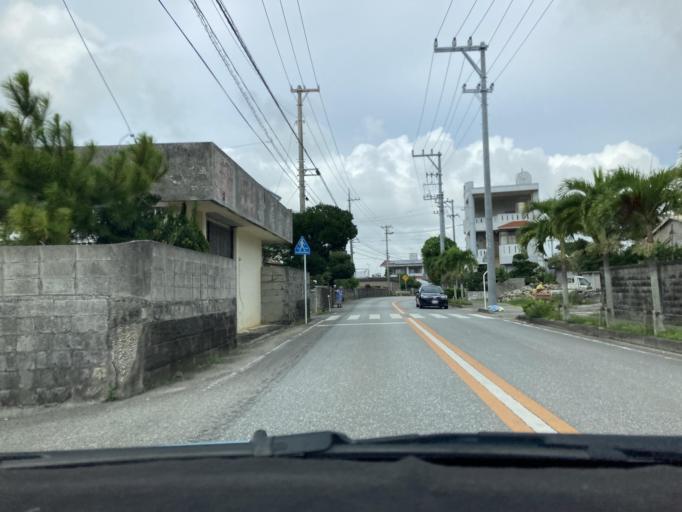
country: JP
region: Okinawa
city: Itoman
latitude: 26.1074
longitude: 127.6650
